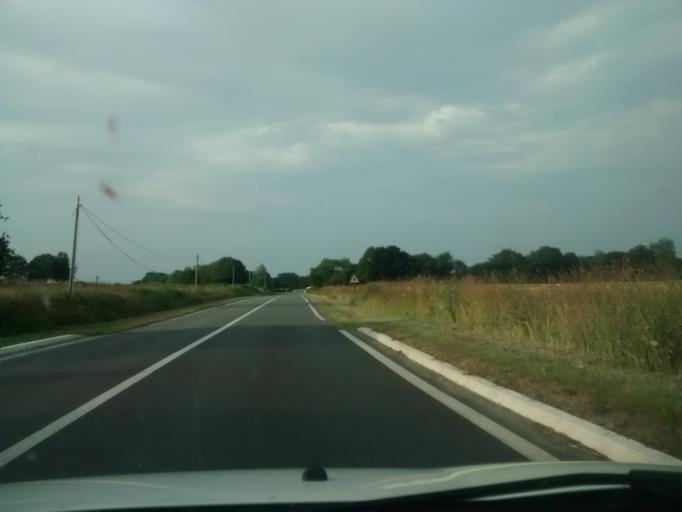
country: FR
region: Brittany
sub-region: Departement des Cotes-d'Armor
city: Saint-Quay-Perros
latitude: 48.7565
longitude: -3.4385
